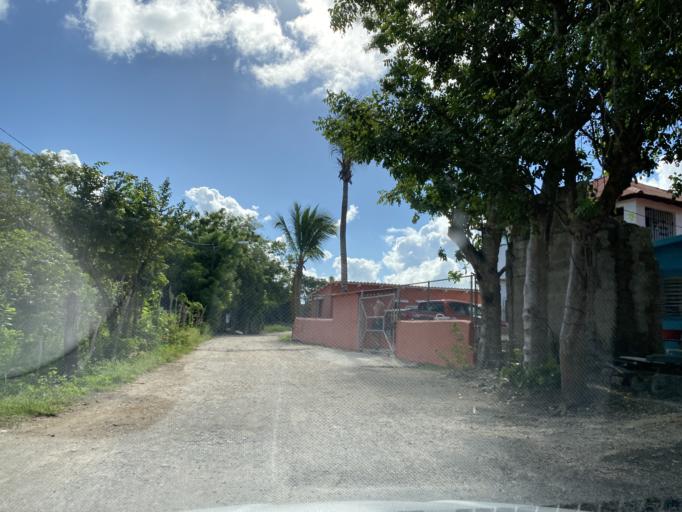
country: DO
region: La Romana
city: La Romana
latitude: 18.3649
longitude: -68.8415
